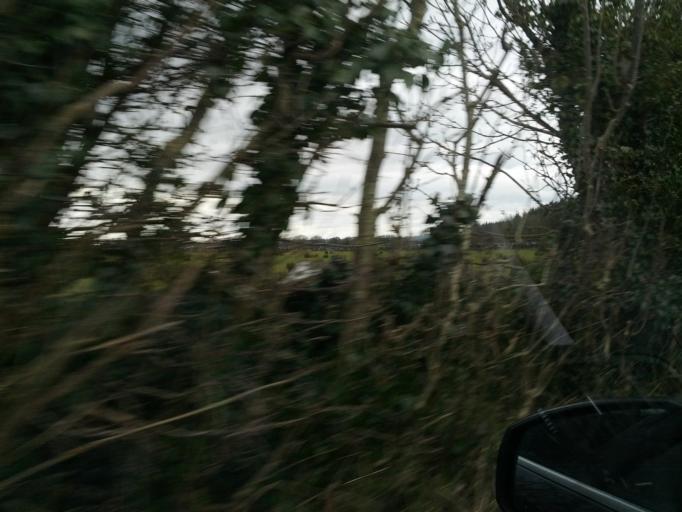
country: IE
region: Connaught
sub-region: County Galway
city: Athenry
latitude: 53.3754
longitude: -8.6343
